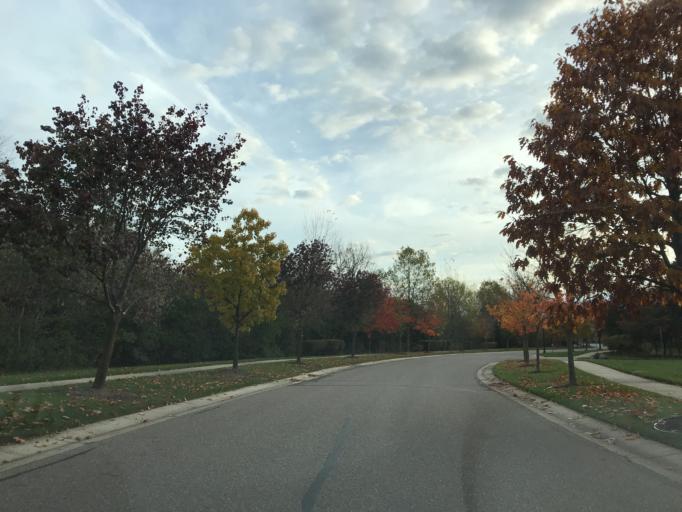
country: US
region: Michigan
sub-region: Oakland County
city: Wixom
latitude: 42.4761
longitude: -83.5378
